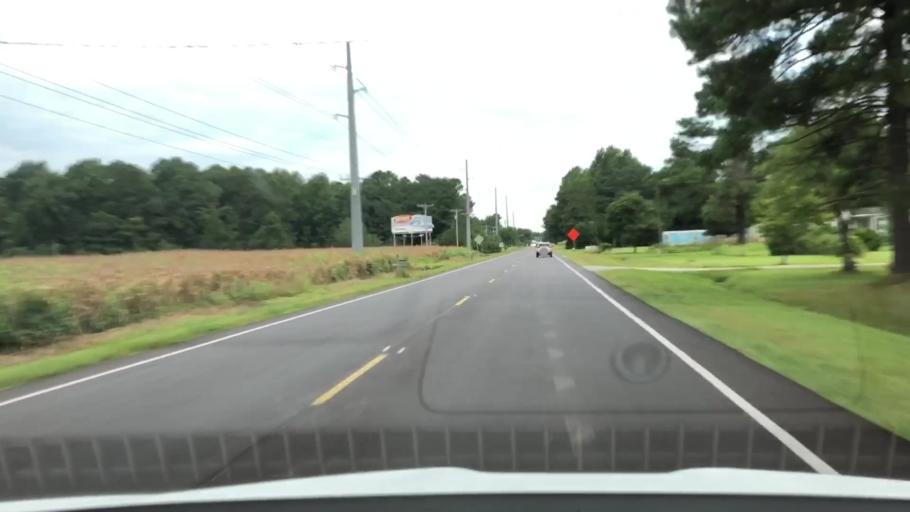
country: US
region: North Carolina
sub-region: Jones County
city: Maysville
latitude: 34.8327
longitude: -77.1635
